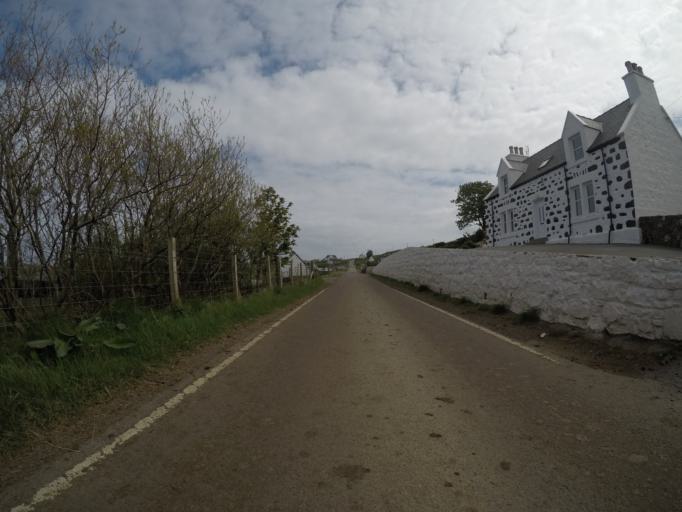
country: GB
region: Scotland
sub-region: Highland
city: Portree
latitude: 57.6846
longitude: -6.3065
